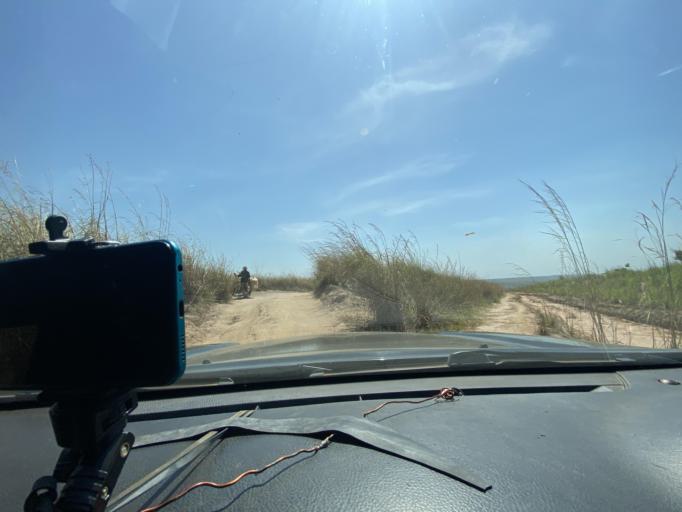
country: CD
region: Kasai-Oriental
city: Kabinda
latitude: -5.9473
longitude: 24.8067
